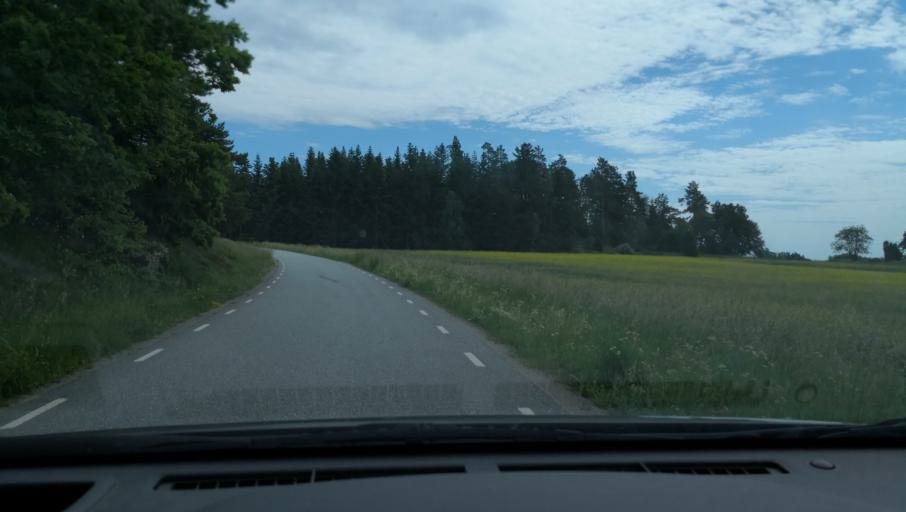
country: SE
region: Uppsala
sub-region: Enkopings Kommun
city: Orsundsbro
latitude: 59.7002
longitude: 17.4291
